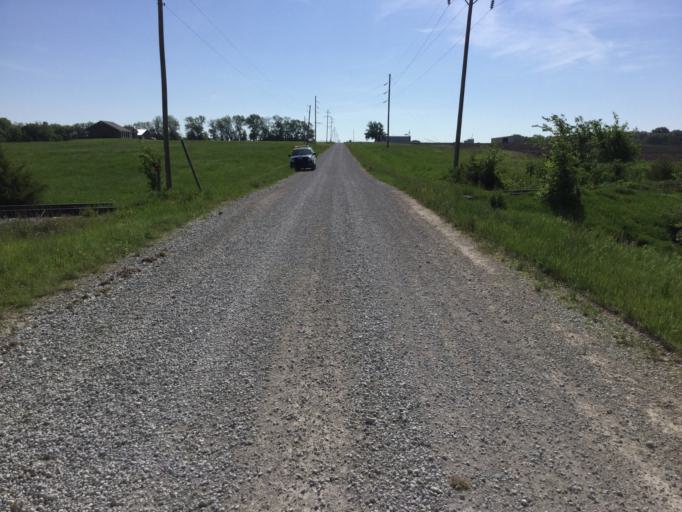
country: US
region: Kansas
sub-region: Coffey County
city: Burlington
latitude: 38.1841
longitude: -95.6243
